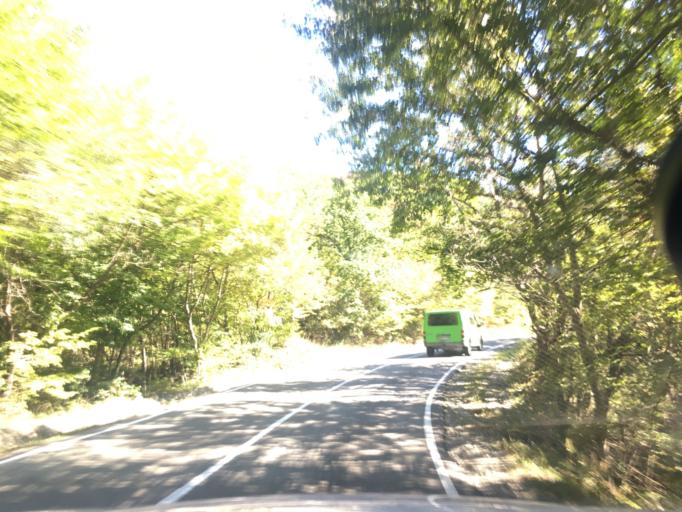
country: GE
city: Didi Lilo
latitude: 41.8616
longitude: 44.9075
